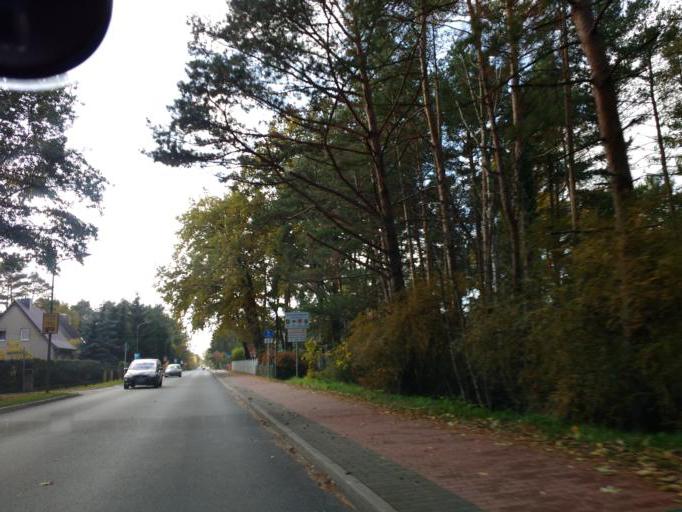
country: DE
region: Brandenburg
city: Petershagen
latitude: 52.5464
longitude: 13.8389
